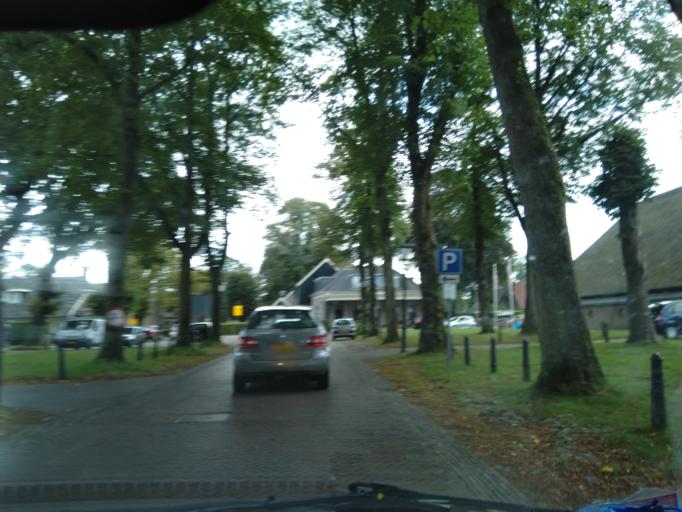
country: NL
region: Drenthe
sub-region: Gemeente Tynaarlo
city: Vries
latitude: 53.0773
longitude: 6.5775
